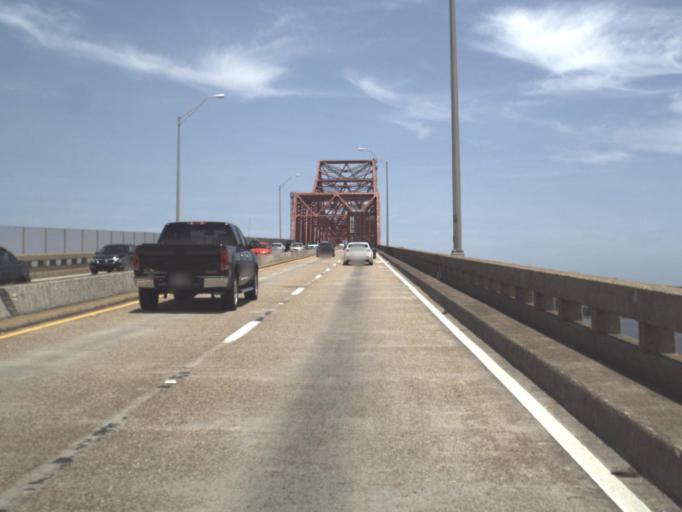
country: US
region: Florida
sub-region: Duval County
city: Jacksonville
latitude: 30.3271
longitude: -81.6290
